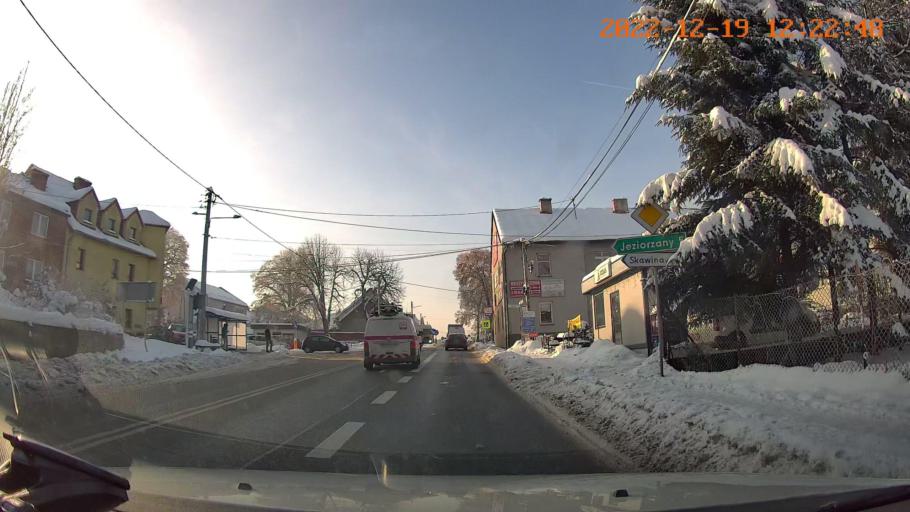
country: PL
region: Lesser Poland Voivodeship
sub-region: Powiat krakowski
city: Liszki
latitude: 50.0389
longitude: 19.7685
